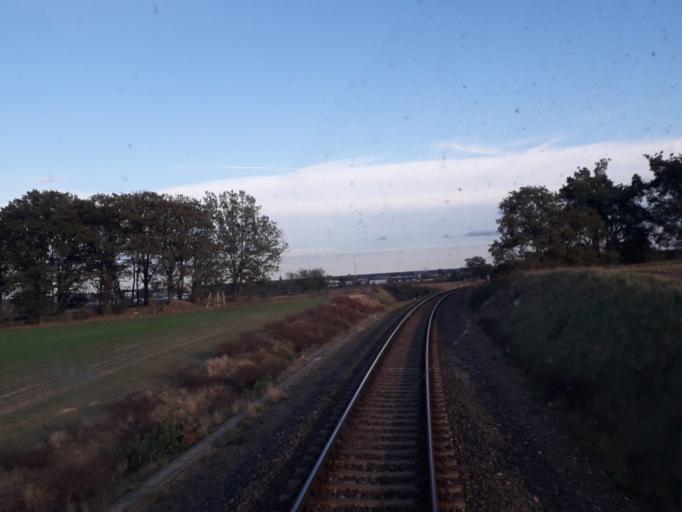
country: DE
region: Brandenburg
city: Wittstock
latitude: 53.1587
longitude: 12.4334
